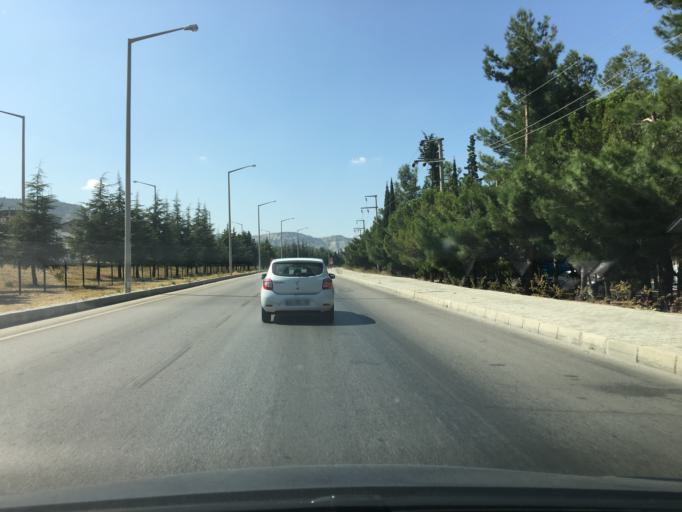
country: TR
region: Burdur
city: Burdur
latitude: 37.7353
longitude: 30.3103
